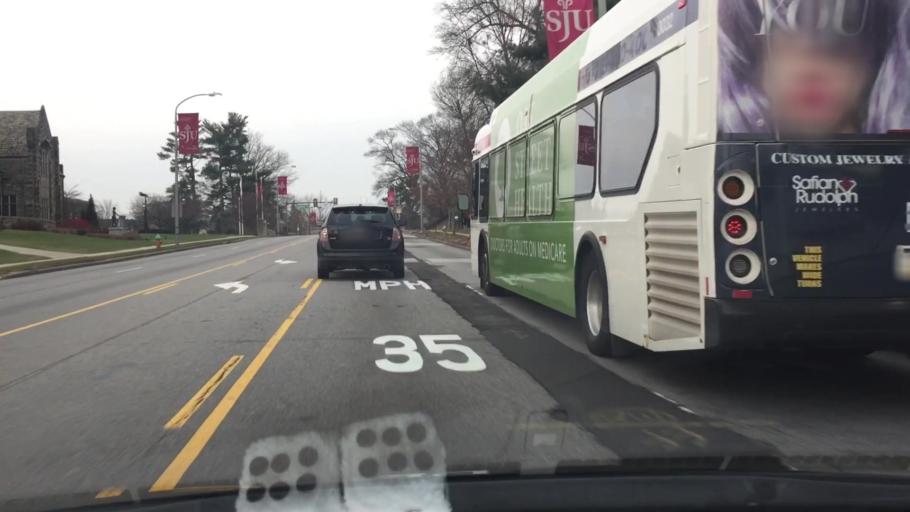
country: US
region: Pennsylvania
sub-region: Montgomery County
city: Bala-Cynwyd
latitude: 39.9961
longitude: -75.2376
